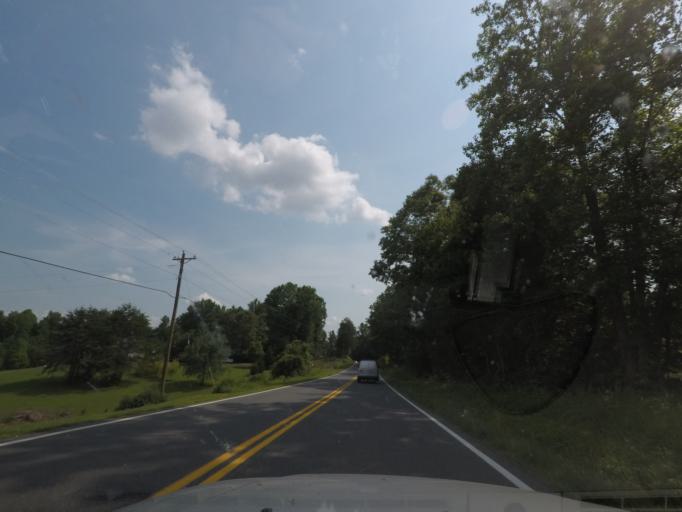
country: US
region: Virginia
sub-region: Fluvanna County
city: Palmyra
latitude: 37.8908
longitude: -78.2624
